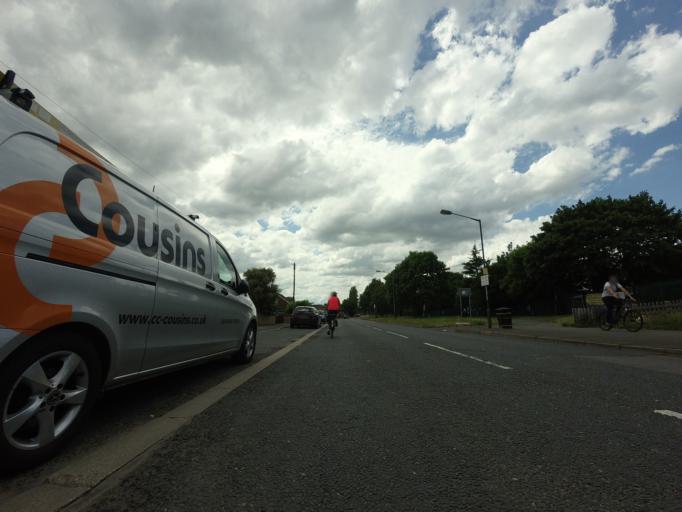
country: GB
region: England
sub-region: Kent
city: Hoo
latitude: 51.4206
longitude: 0.5518
